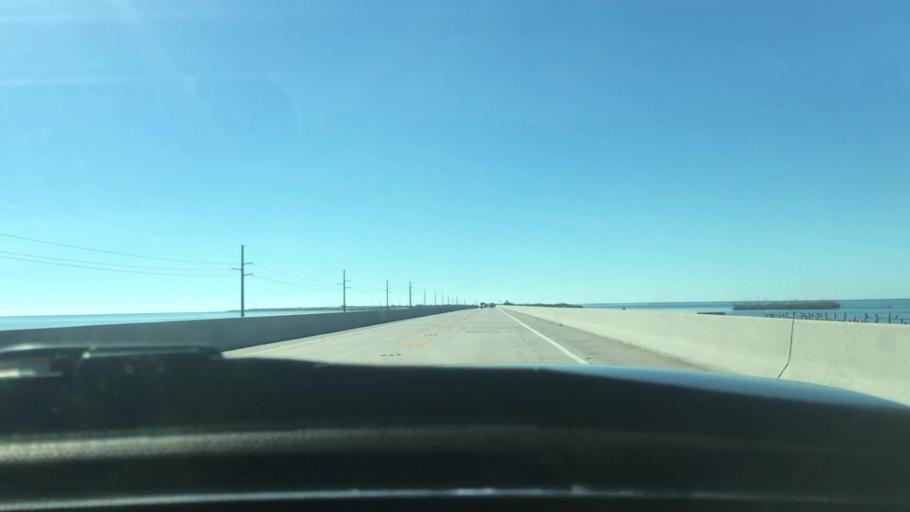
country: US
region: Florida
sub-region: Monroe County
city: Marathon
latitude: 24.6855
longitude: -81.2172
